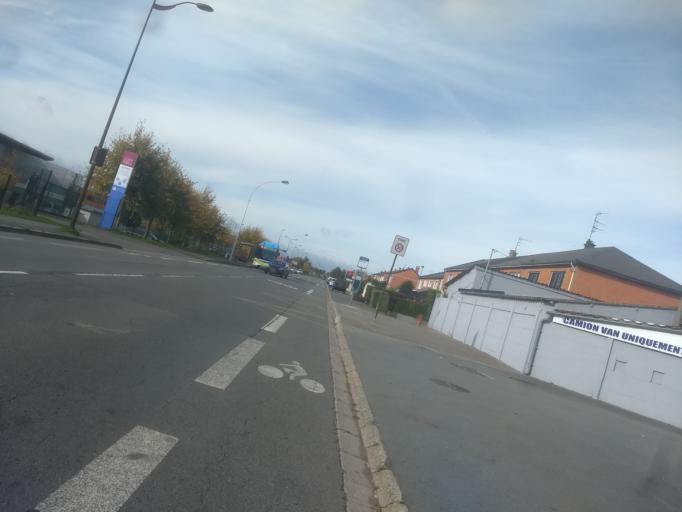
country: FR
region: Nord-Pas-de-Calais
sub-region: Departement du Pas-de-Calais
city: Dainville
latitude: 50.2924
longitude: 2.7341
